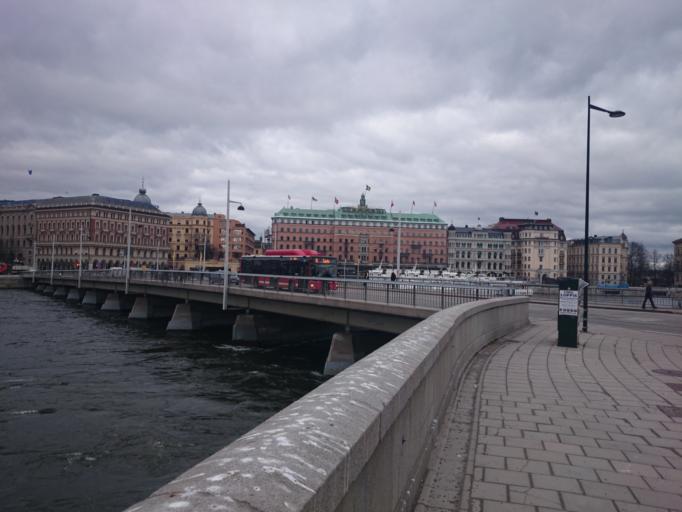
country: SE
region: Stockholm
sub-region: Stockholms Kommun
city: Stockholm
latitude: 59.3281
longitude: 18.0725
